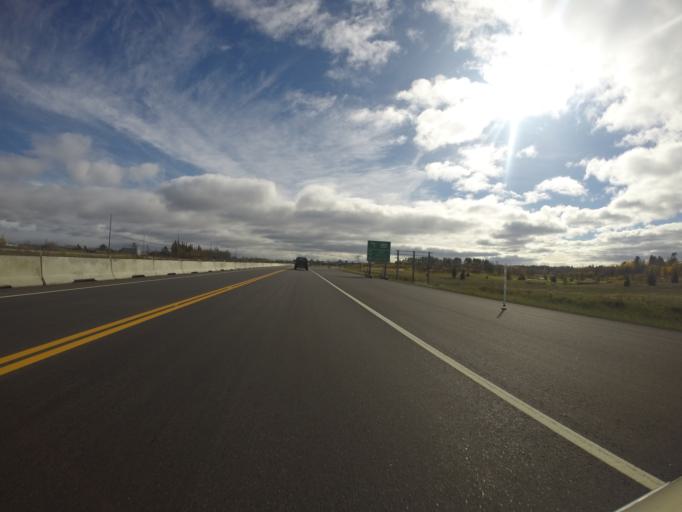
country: CA
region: Ontario
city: Greater Sudbury
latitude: 46.1093
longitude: -80.6697
